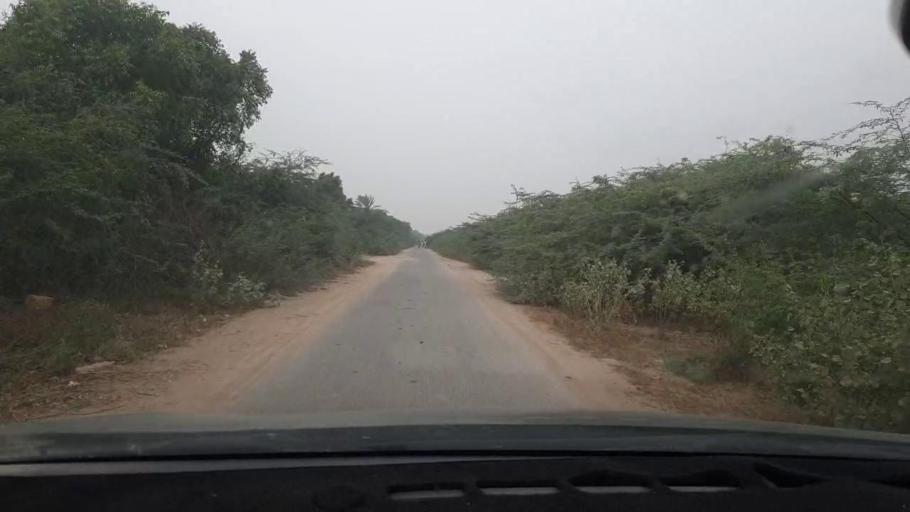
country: PK
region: Sindh
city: Malir Cantonment
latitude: 24.9255
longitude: 67.3249
